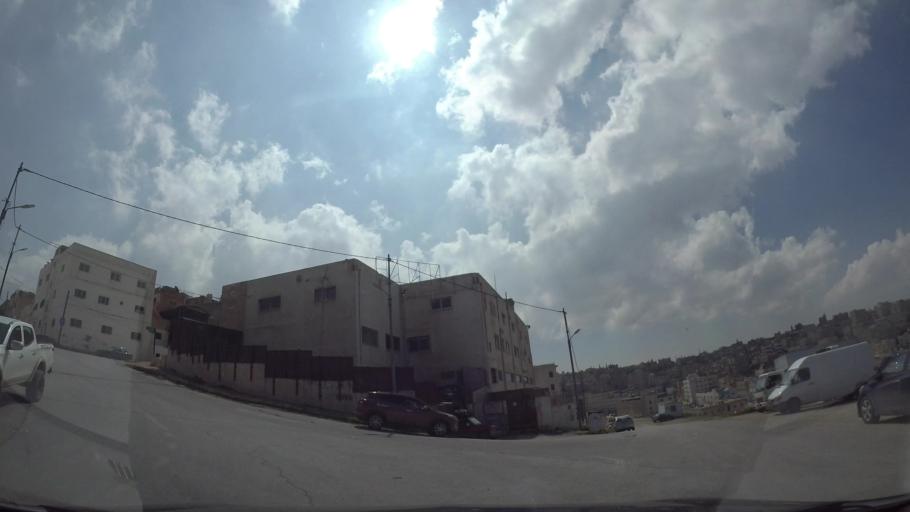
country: JO
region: Zarqa
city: Russeifa
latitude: 31.9909
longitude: 35.9952
